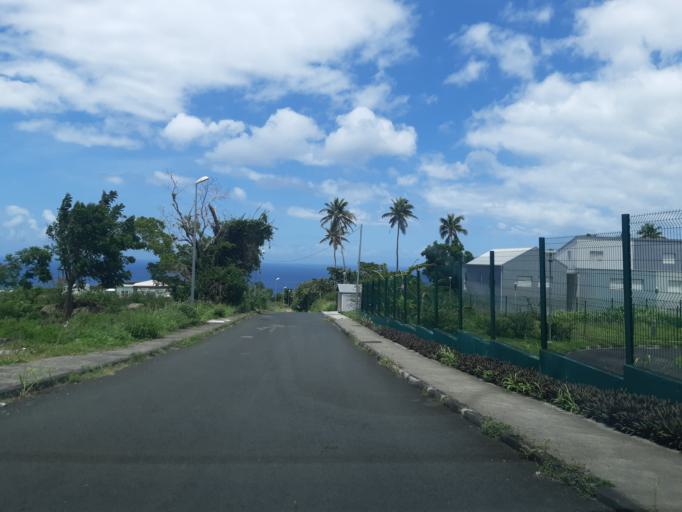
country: GP
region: Guadeloupe
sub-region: Guadeloupe
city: Basse-Terre
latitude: 16.0097
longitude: -61.7144
